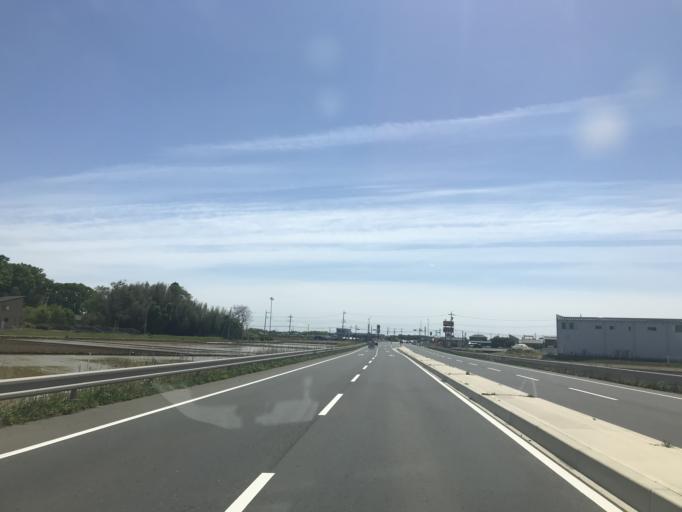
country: JP
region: Ibaraki
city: Ishige
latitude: 36.1657
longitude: 139.9942
